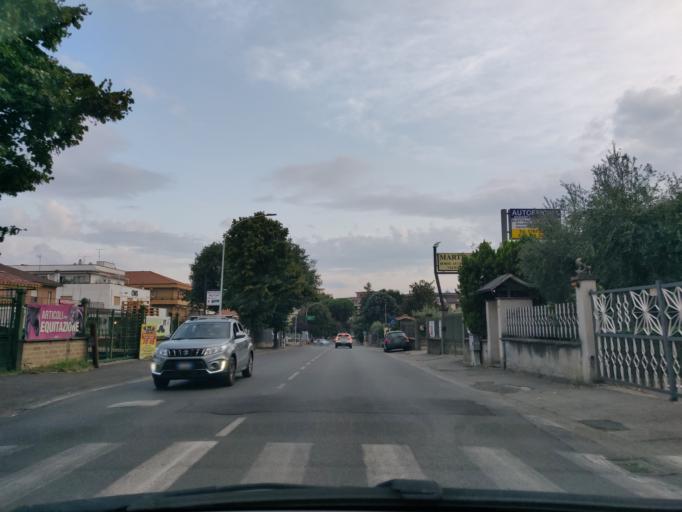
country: IT
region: Latium
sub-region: Provincia di Viterbo
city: Viterbo
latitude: 42.4296
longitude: 12.1001
